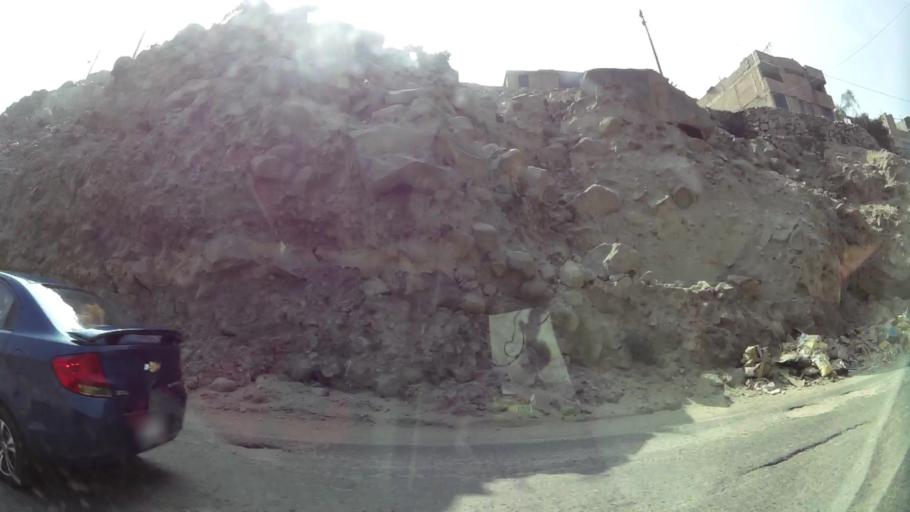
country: PE
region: Lima
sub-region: Provincia de Huarochiri
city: Ricardo Palma
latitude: -11.9238
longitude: -76.6813
